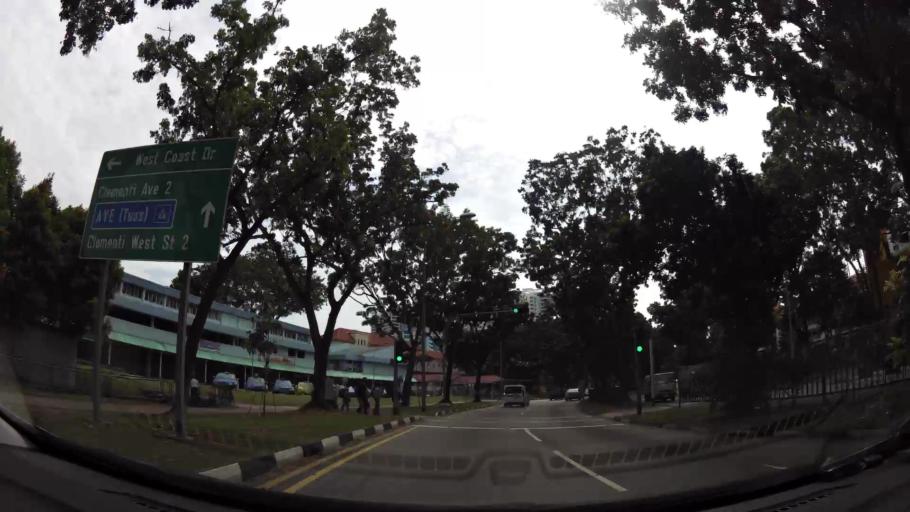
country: SG
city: Singapore
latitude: 1.3112
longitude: 103.7580
